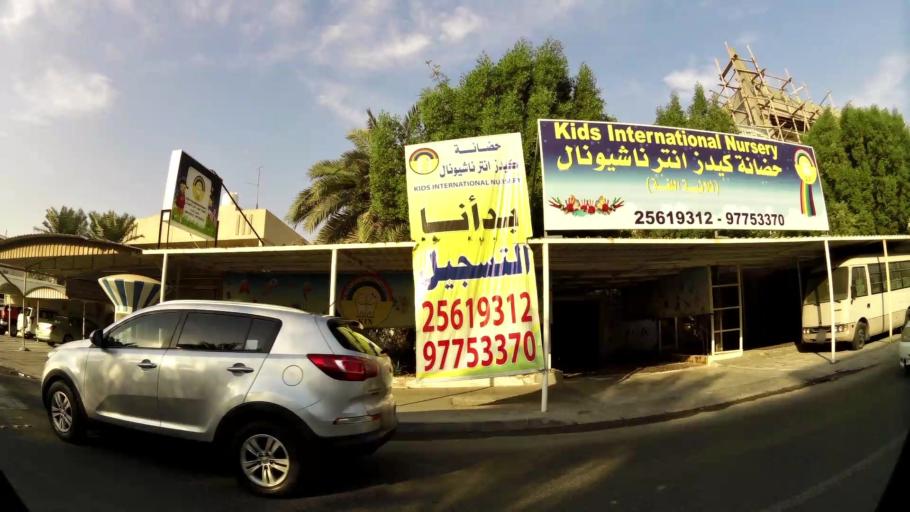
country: KW
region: Muhafazat Hawalli
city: Ar Rumaythiyah
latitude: 29.3207
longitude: 48.0726
